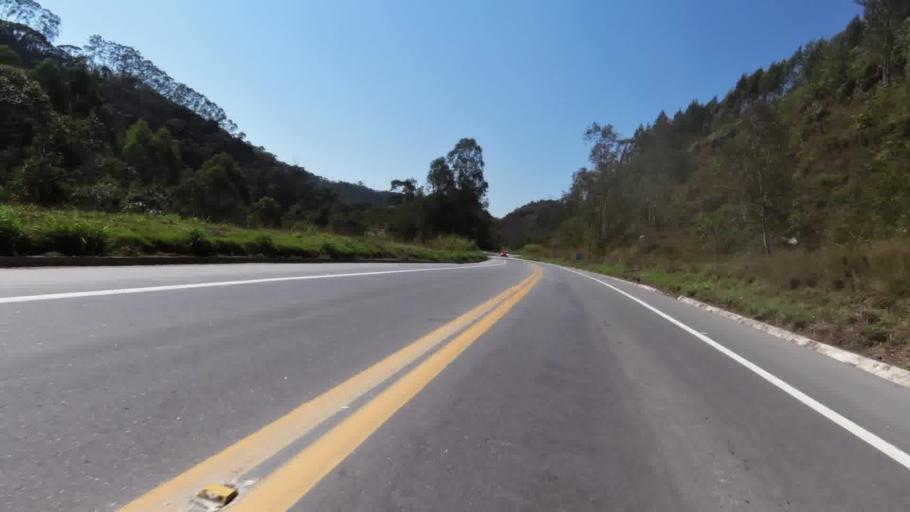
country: BR
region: Espirito Santo
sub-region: Marechal Floriano
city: Marechal Floriano
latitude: -20.4143
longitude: -40.8422
